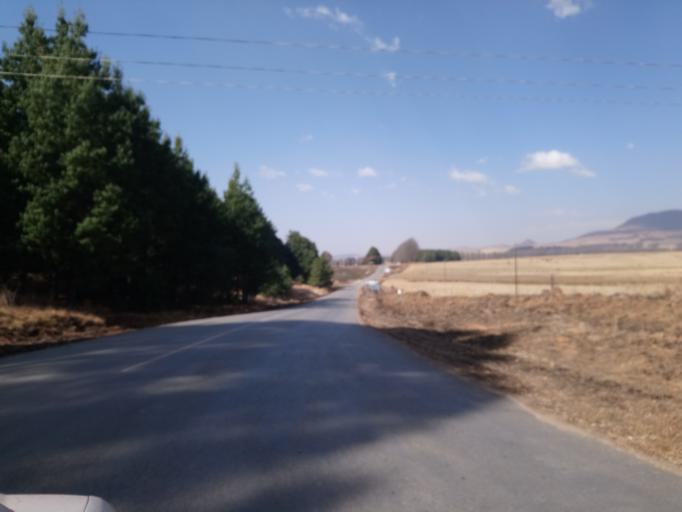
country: ZA
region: KwaZulu-Natal
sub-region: uMgungundlovu District Municipality
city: Mooirivier
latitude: -29.3217
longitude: 29.7204
